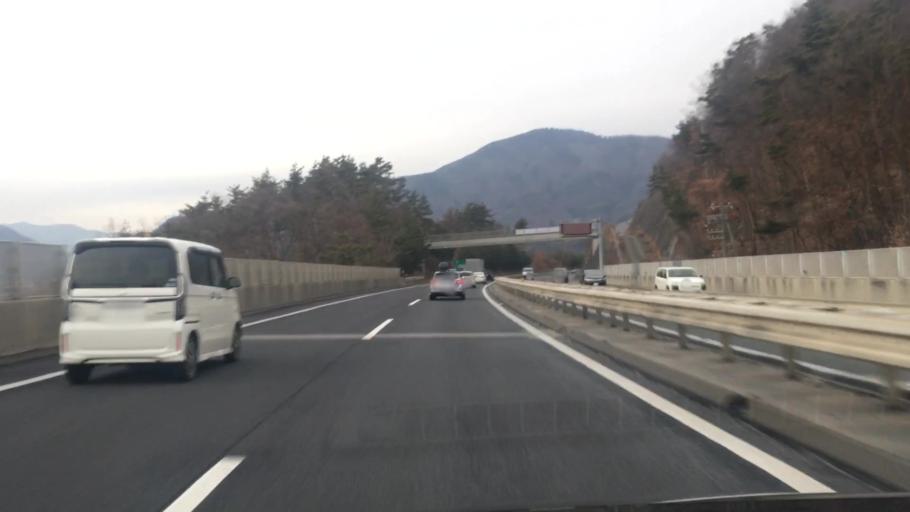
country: JP
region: Nagano
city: Ueda
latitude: 36.4483
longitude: 138.2032
